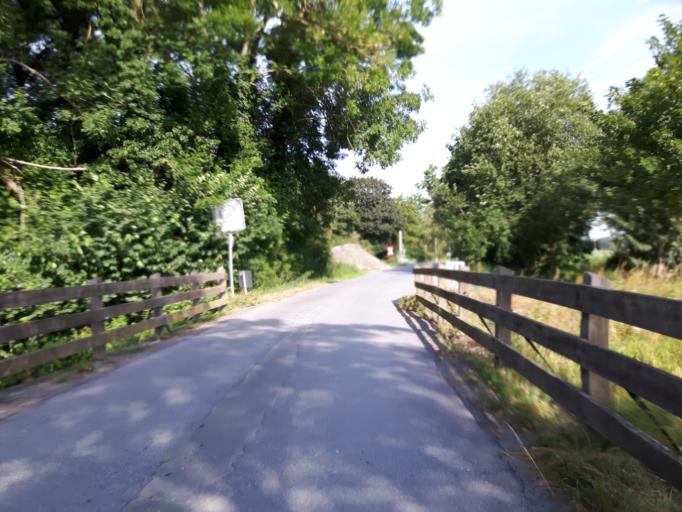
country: DE
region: Lower Saxony
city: Elsfleth
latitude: 53.2001
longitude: 8.4768
